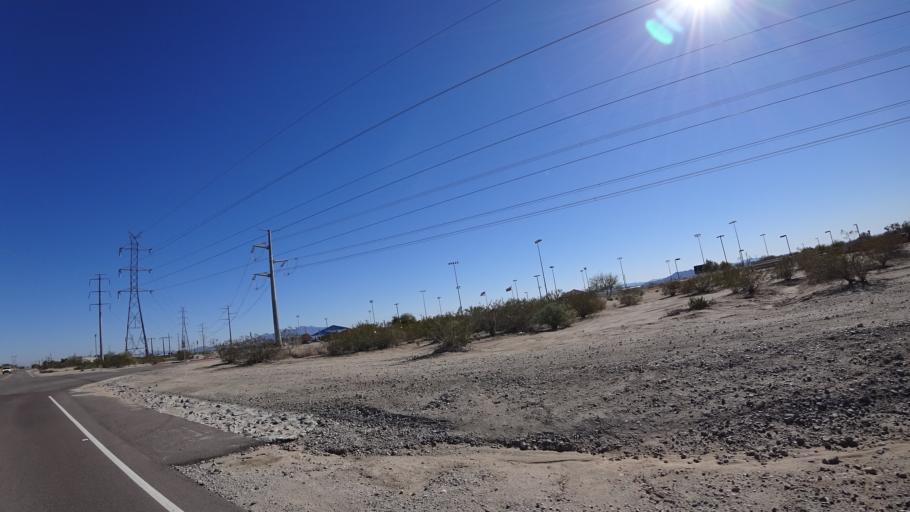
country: US
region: Arizona
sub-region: Maricopa County
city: Buckeye
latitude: 33.4213
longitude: -112.5431
